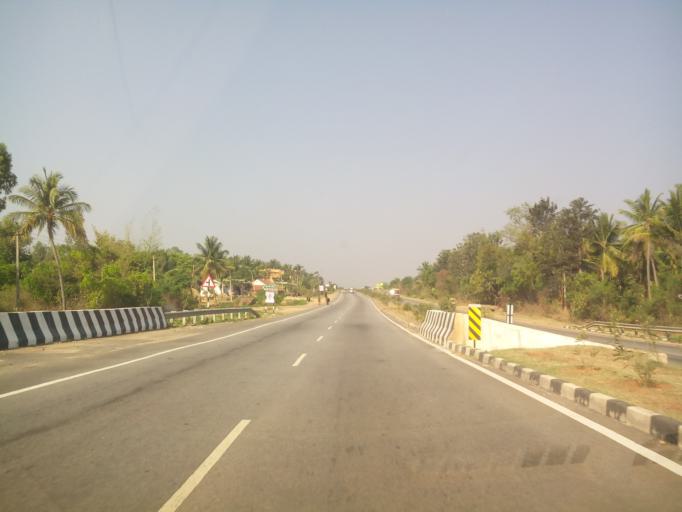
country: IN
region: Karnataka
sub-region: Tumkur
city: Kunigal
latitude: 13.0388
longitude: 77.1038
